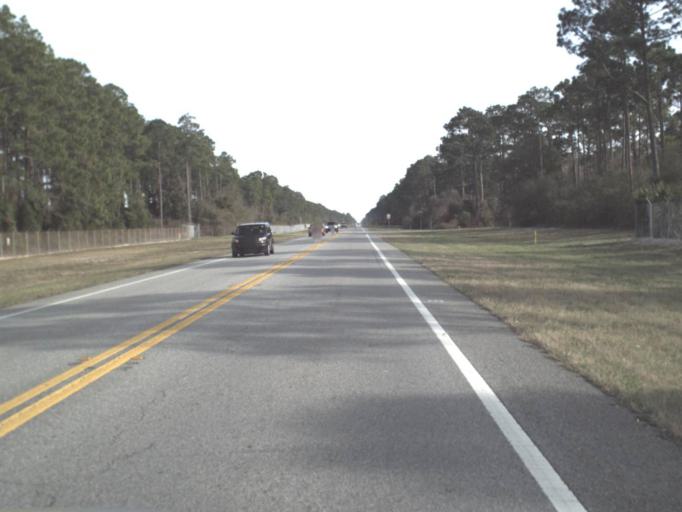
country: US
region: Florida
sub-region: Bay County
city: Tyndall Air Force Base
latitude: 30.0602
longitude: -85.5776
